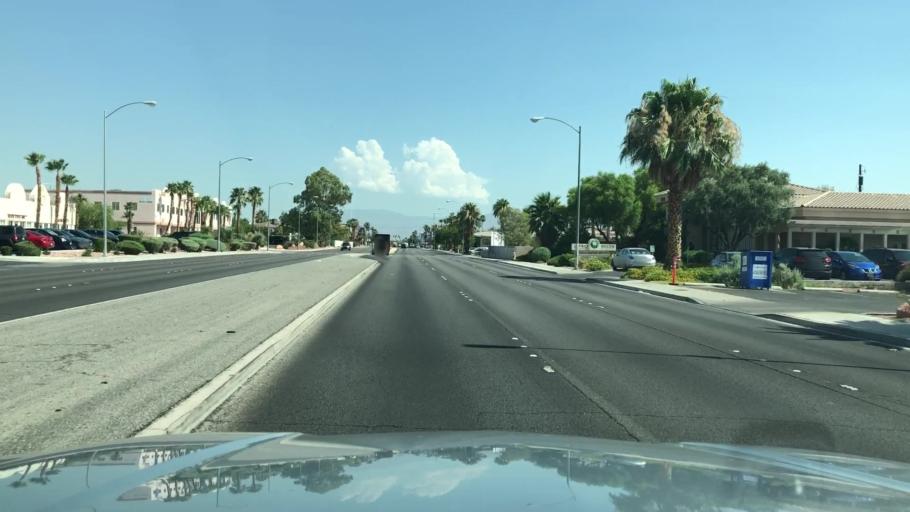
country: US
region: Nevada
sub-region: Clark County
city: Spring Valley
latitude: 36.1392
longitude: -115.2251
